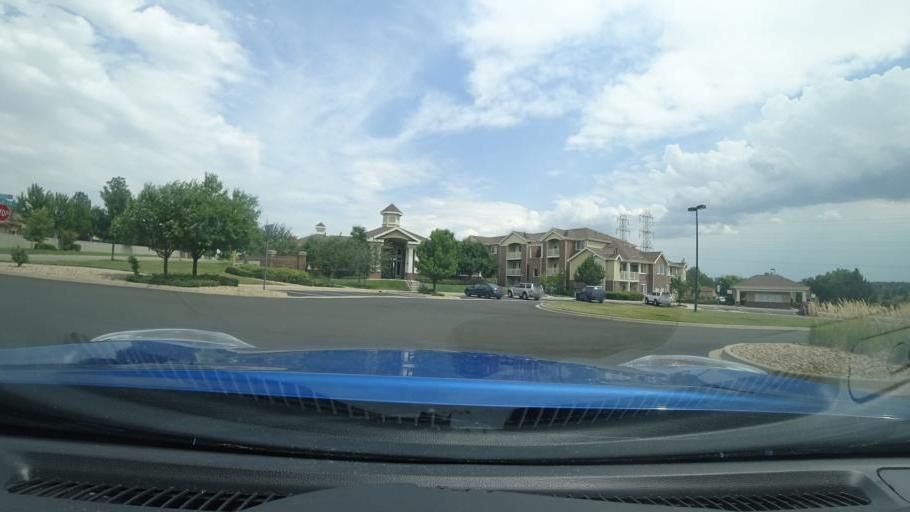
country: US
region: Colorado
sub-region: Adams County
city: Aurora
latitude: 39.6688
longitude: -104.7633
